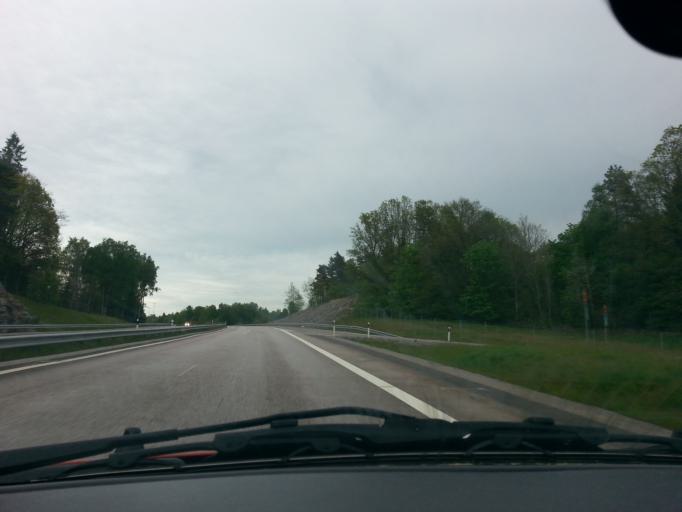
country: SE
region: Vaestra Goetaland
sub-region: Alingsas Kommun
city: Ingared
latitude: 57.8671
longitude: 12.4880
